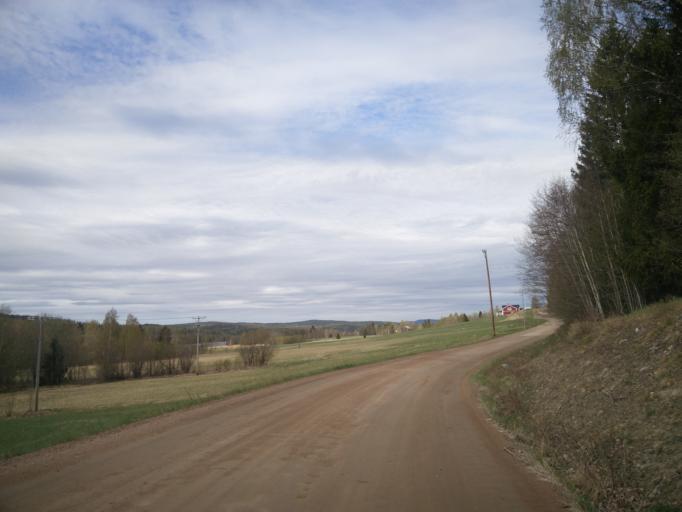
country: SE
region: Vaesternorrland
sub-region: Sundsvalls Kommun
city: Vi
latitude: 62.2724
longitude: 17.1579
